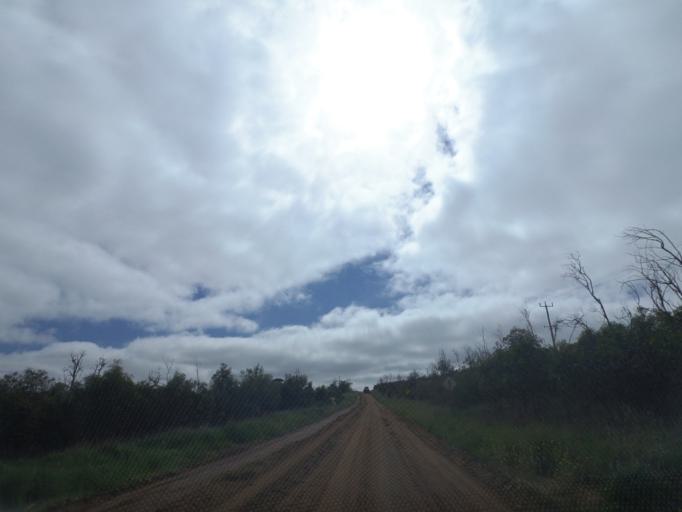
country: AU
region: Victoria
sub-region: Hume
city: Craigieburn
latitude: -37.5040
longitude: 144.8980
